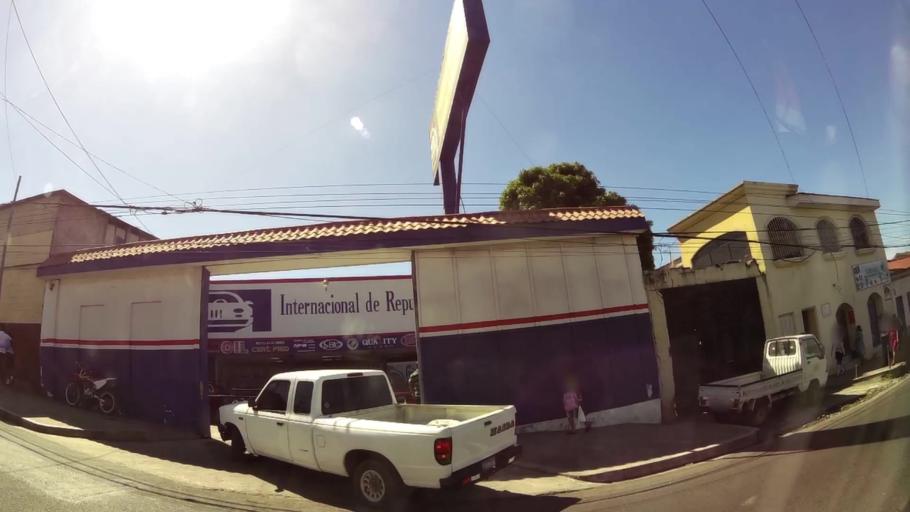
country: SV
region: Ahuachapan
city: Ahuachapan
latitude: 13.9244
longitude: -89.8491
